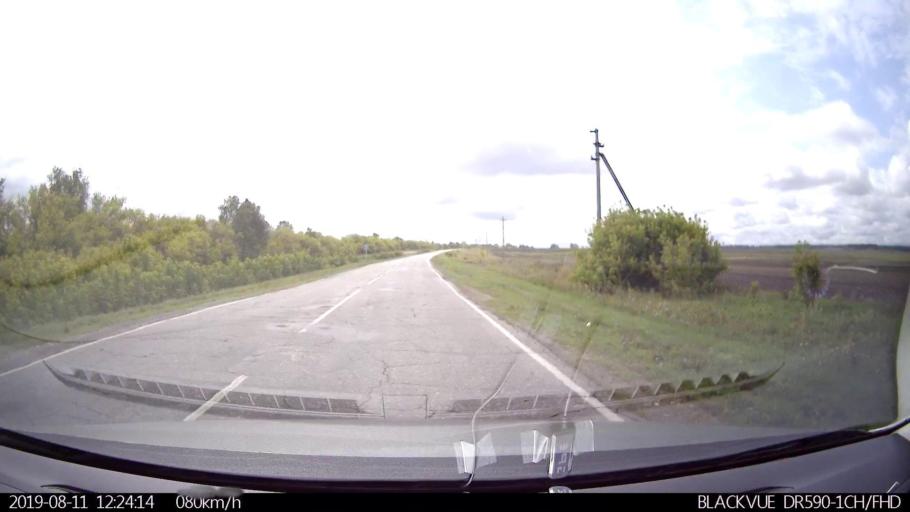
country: RU
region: Ulyanovsk
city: Ignatovka
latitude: 53.8857
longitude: 47.9497
